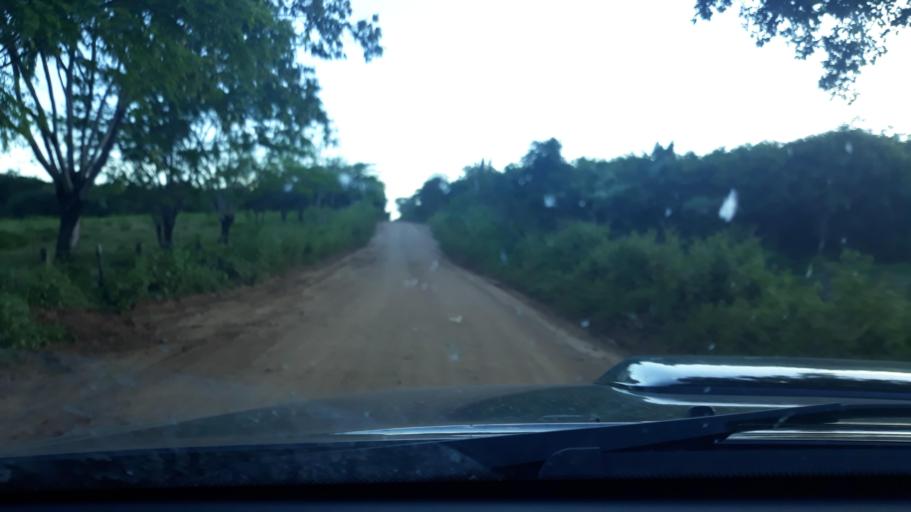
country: BR
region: Bahia
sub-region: Riacho De Santana
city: Riacho de Santana
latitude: -13.8145
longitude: -42.7226
